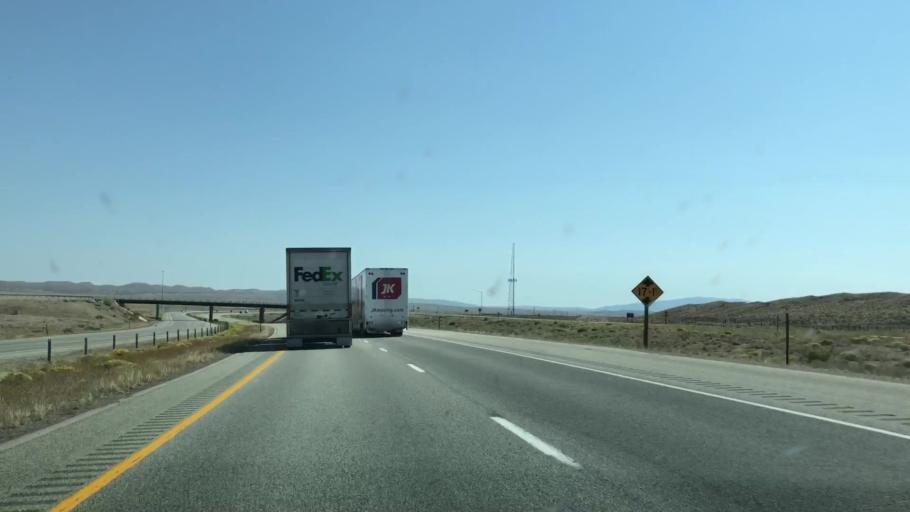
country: US
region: Wyoming
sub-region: Carbon County
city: Rawlins
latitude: 41.7715
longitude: -107.0858
